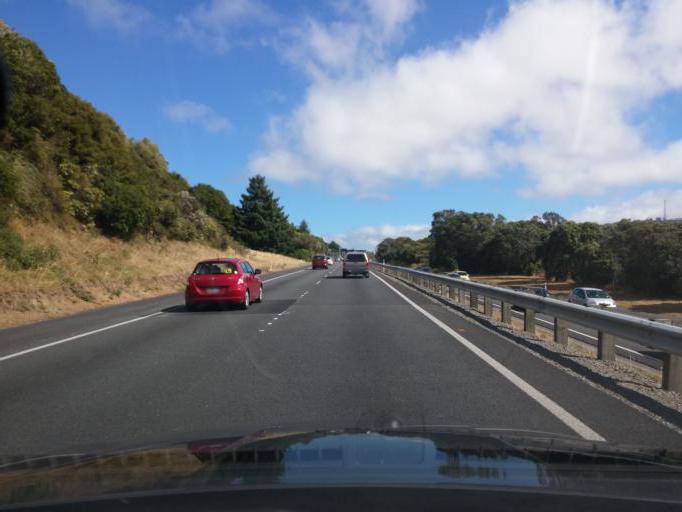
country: NZ
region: Wellington
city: Petone
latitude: -41.2135
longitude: 174.8139
